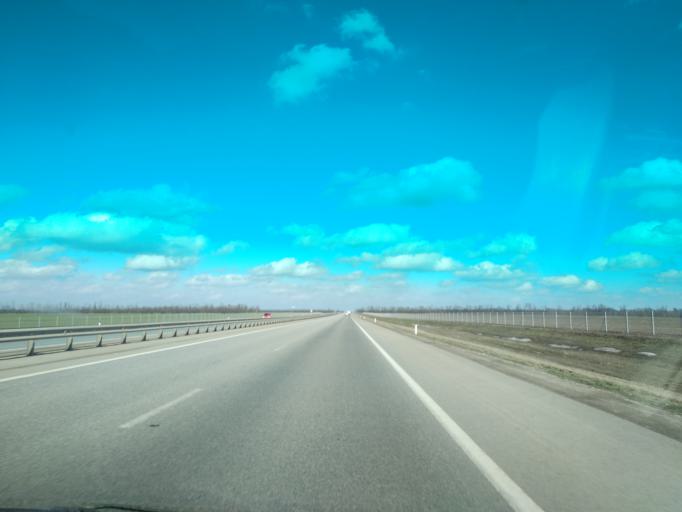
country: RU
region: Krasnodarskiy
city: Berezanskaya
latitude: 45.5914
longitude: 39.5204
